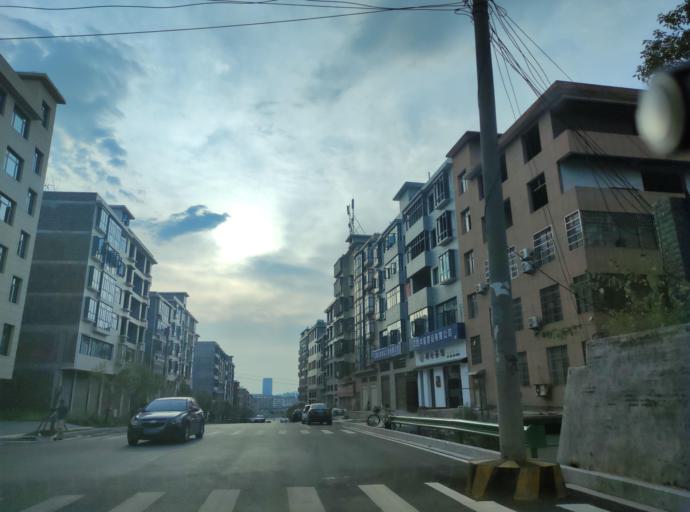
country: CN
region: Jiangxi Sheng
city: Pingxiang
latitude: 27.6434
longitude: 113.8807
